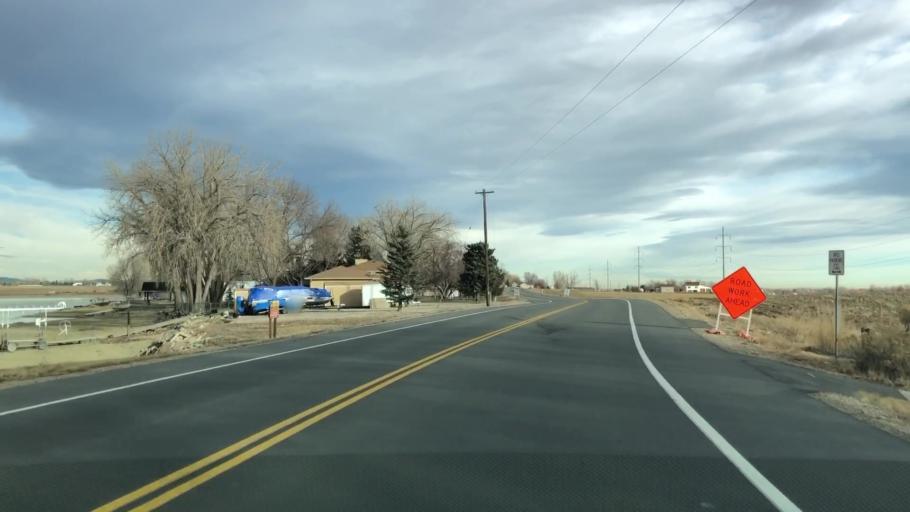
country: US
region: Colorado
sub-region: Larimer County
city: Loveland
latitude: 40.4416
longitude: -105.0457
